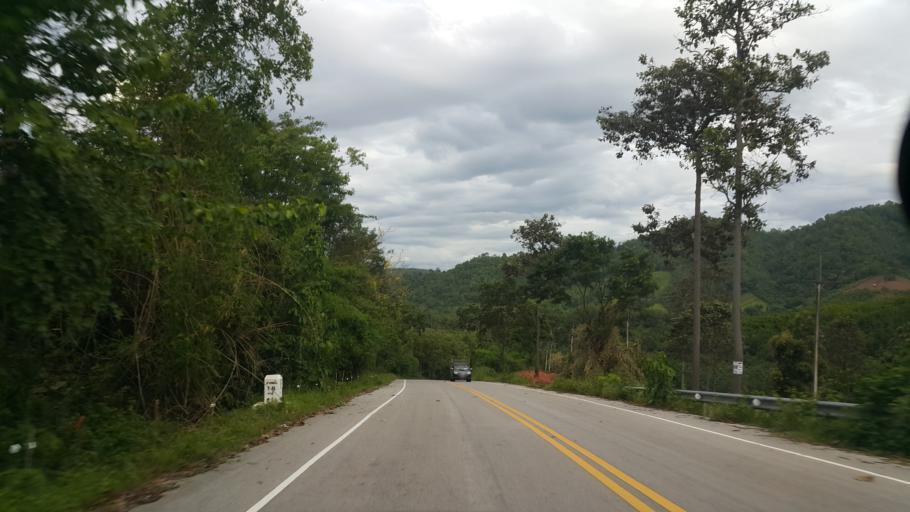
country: TH
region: Loei
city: Na Haeo
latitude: 17.5006
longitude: 101.0915
